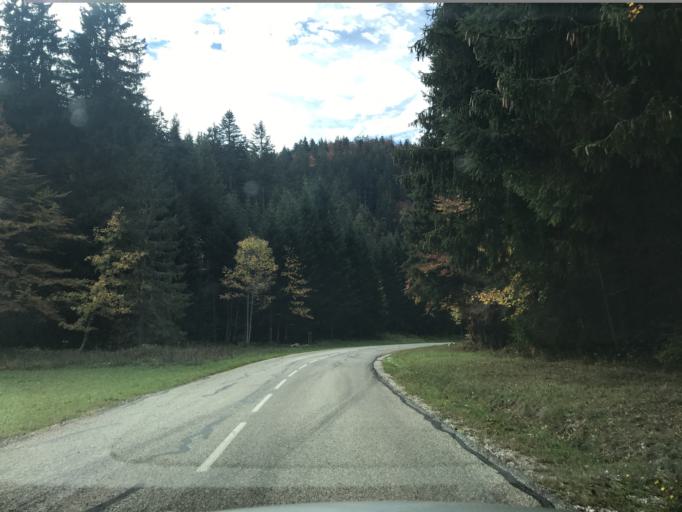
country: FR
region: Rhone-Alpes
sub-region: Departement de la Savoie
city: Vimines
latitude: 45.4537
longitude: 5.8582
